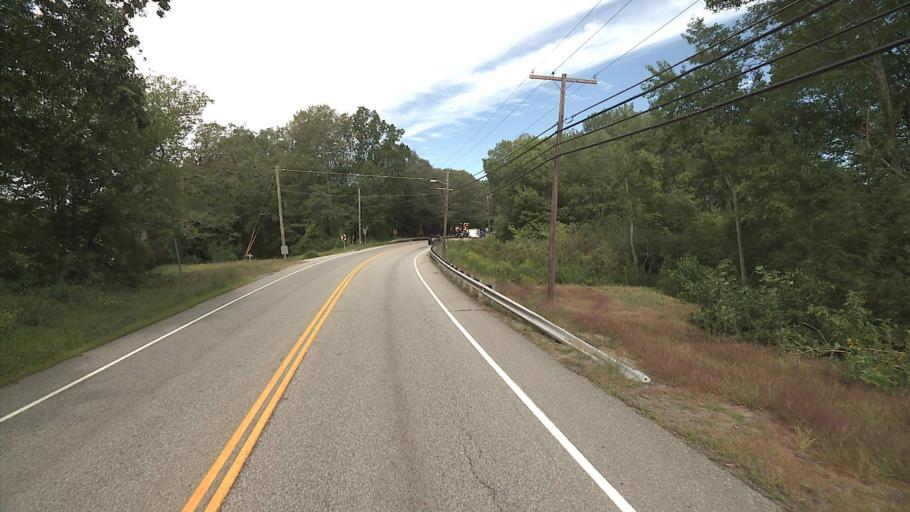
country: US
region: Connecticut
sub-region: Tolland County
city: Mansfield City
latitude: 41.7342
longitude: -72.2544
